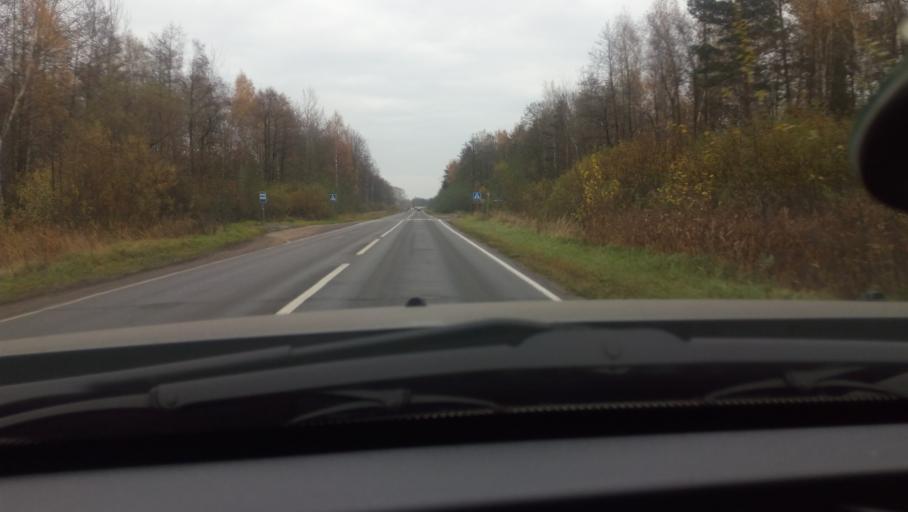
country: RU
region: Moskovskaya
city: Likino-Dulevo
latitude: 55.6997
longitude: 38.9264
